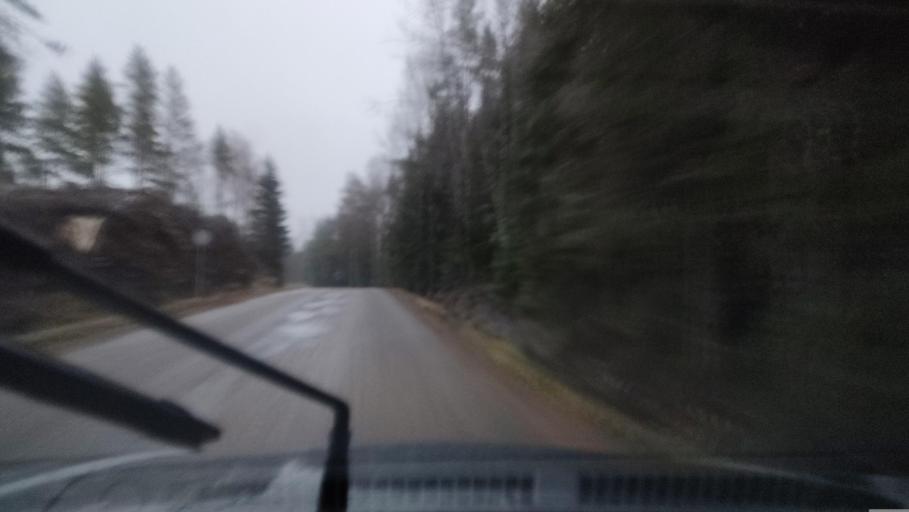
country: FI
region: Southern Ostrobothnia
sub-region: Suupohja
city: Karijoki
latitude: 62.1472
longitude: 21.5580
